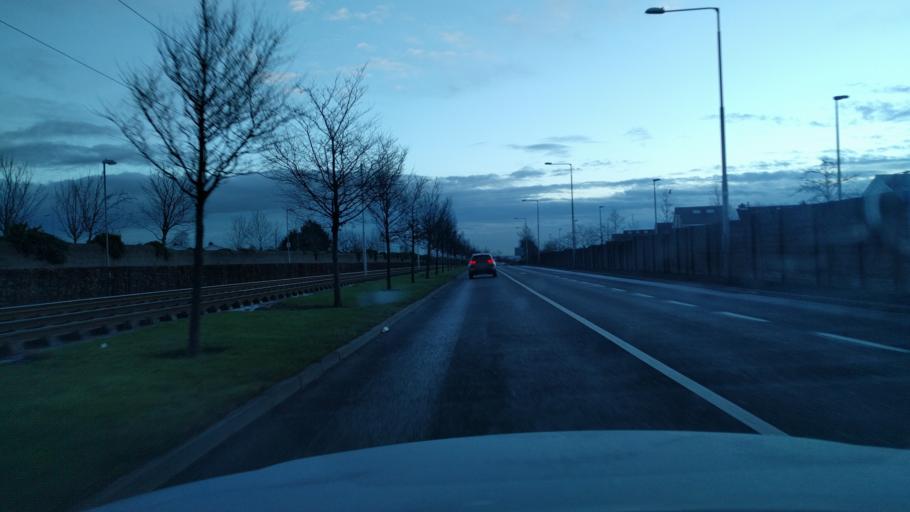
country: IE
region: Leinster
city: Tallaght
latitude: 53.3010
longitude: -6.3720
